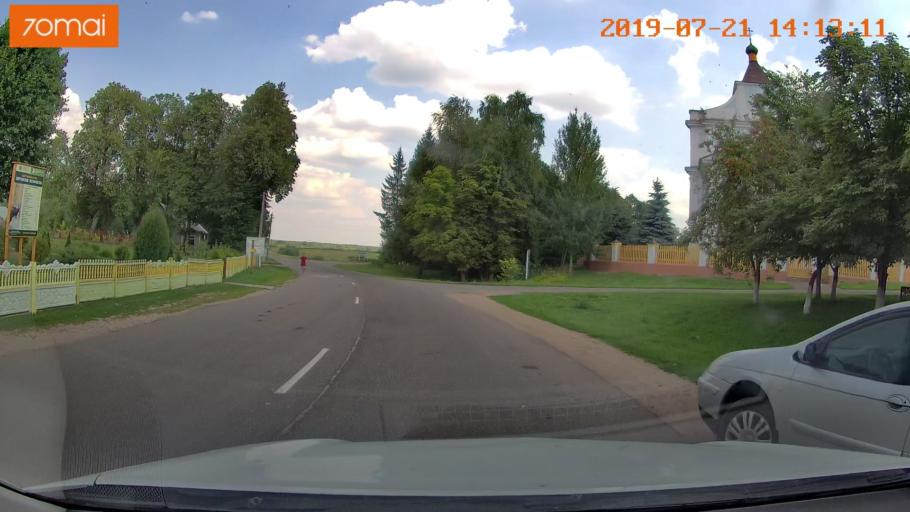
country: BY
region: Grodnenskaya
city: Karelichy
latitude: 53.6508
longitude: 26.1734
